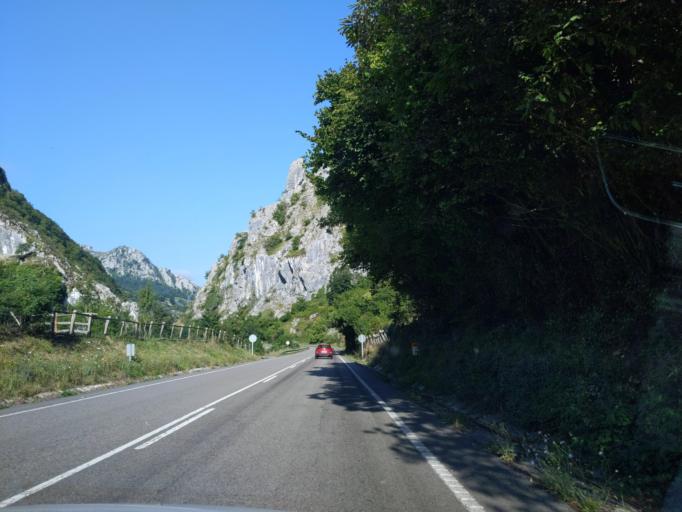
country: ES
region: Asturias
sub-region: Province of Asturias
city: Pola de Laviana
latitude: 43.2324
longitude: -5.4826
